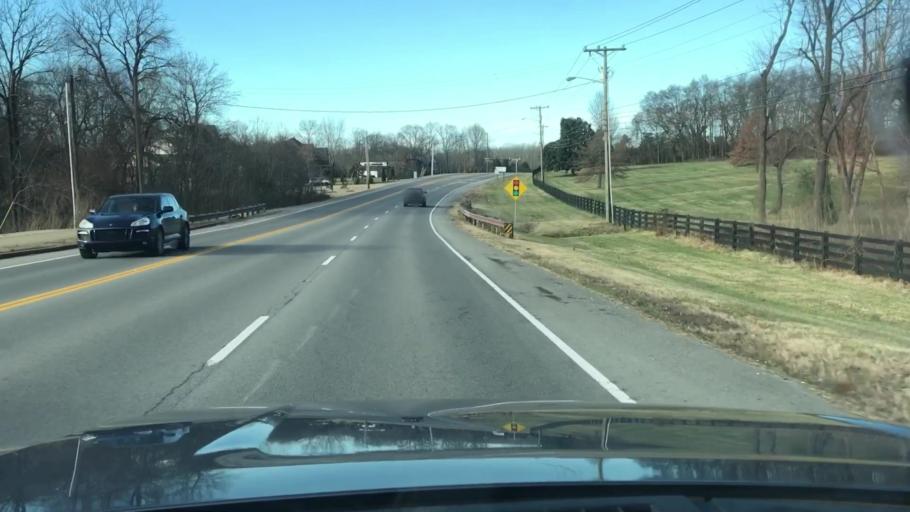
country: US
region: Tennessee
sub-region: Williamson County
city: Brentwood Estates
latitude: 35.9748
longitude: -86.7761
